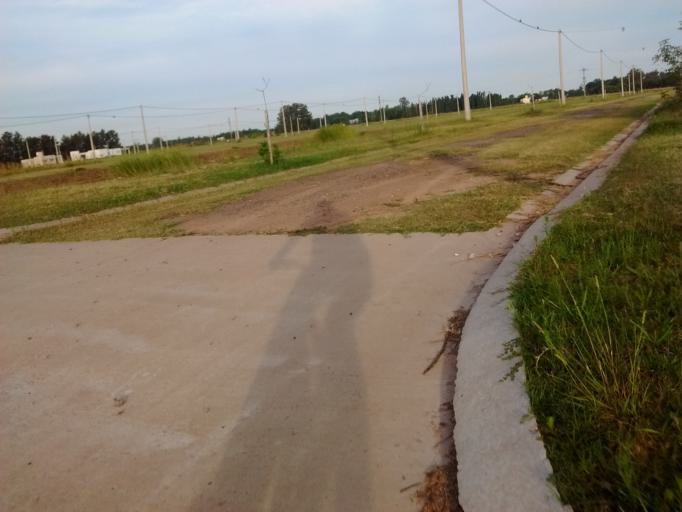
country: AR
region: Santa Fe
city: Roldan
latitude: -32.9293
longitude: -60.8747
